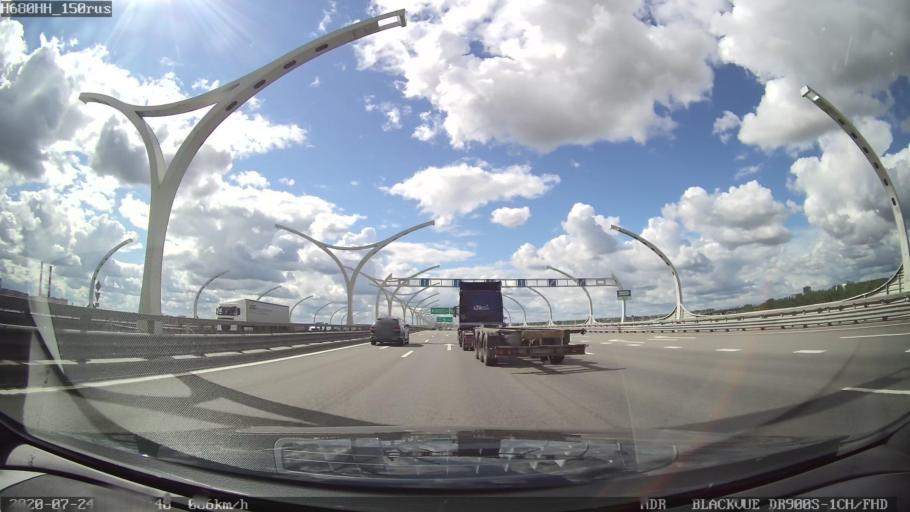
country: RU
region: St.-Petersburg
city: Dachnoye
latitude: 59.8401
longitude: 30.2818
